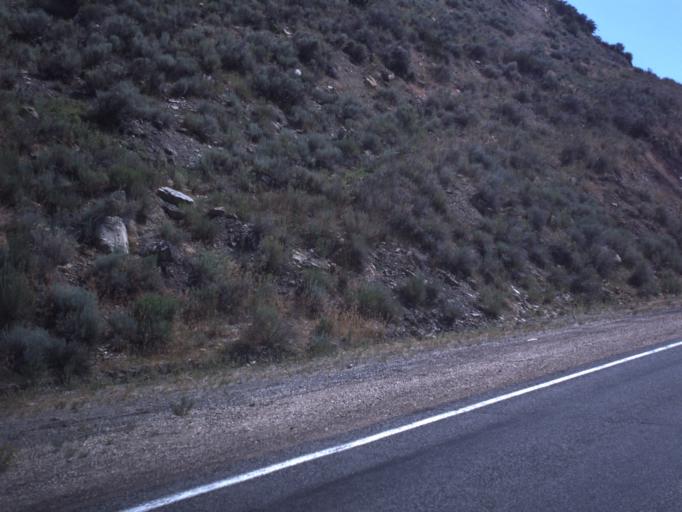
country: US
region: Utah
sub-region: Sanpete County
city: Fairview
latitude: 39.6481
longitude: -111.3806
